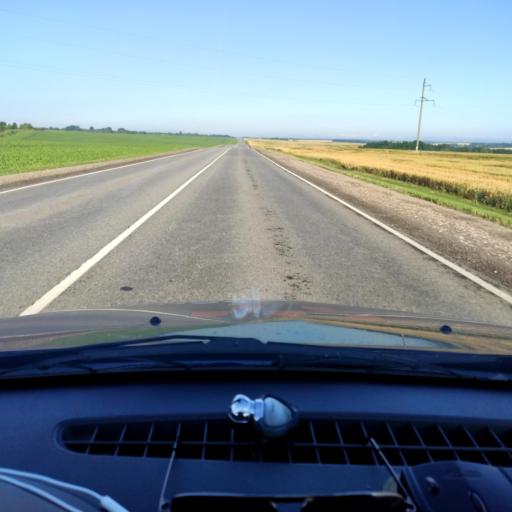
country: RU
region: Orjol
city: Livny
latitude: 52.4354
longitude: 37.3885
